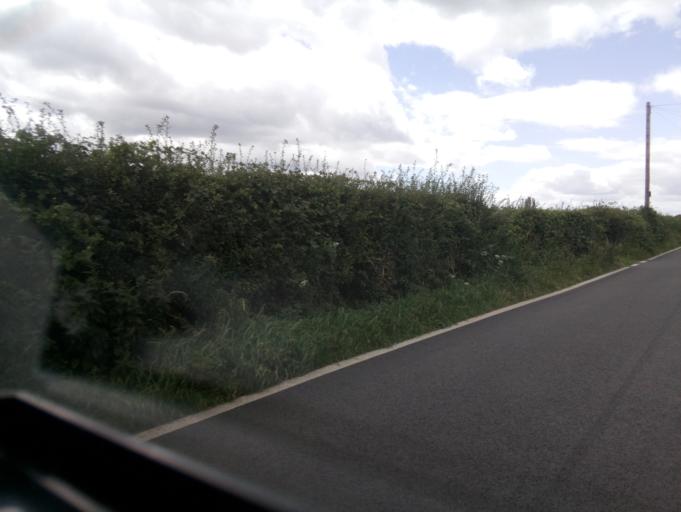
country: GB
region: England
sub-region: Nottinghamshire
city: West Bridgford
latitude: 52.9286
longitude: -1.0925
